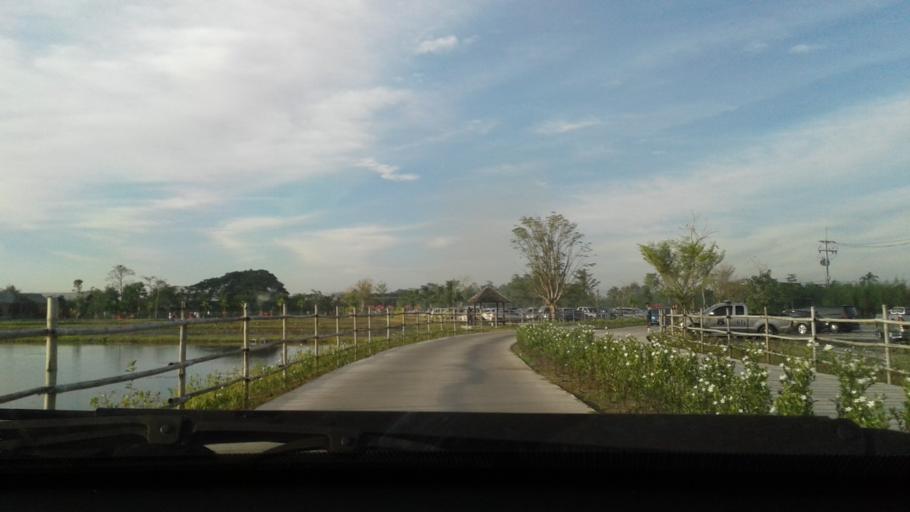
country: TH
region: Nakhon Pathom
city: Nakhon Chai Si
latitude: 13.8974
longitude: 100.2349
